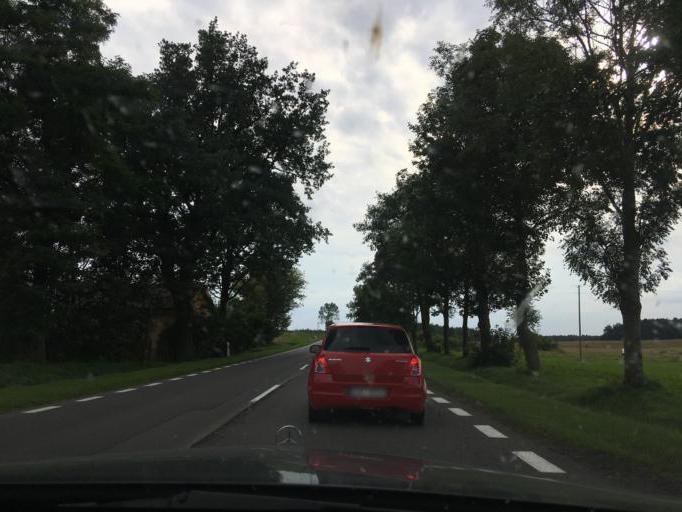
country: PL
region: Podlasie
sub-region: Powiat kolnenski
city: Stawiski
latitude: 53.4546
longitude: 22.1905
